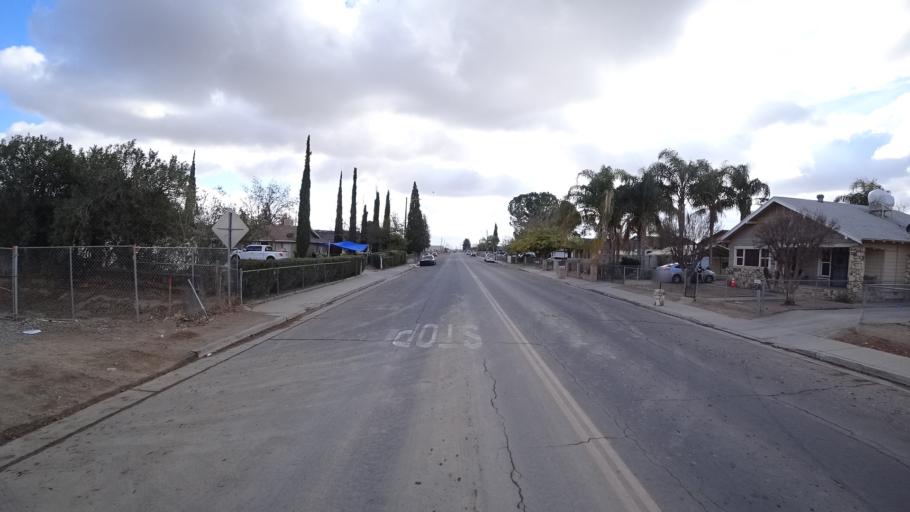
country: US
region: California
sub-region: Kern County
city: Bakersfield
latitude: 35.3599
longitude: -118.9586
